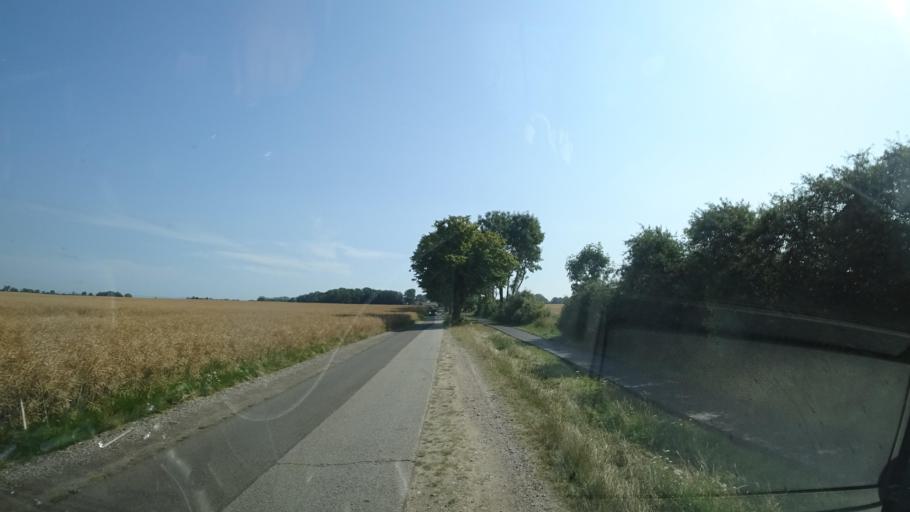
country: DE
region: Mecklenburg-Vorpommern
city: Kemnitz
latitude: 54.1164
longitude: 13.5384
